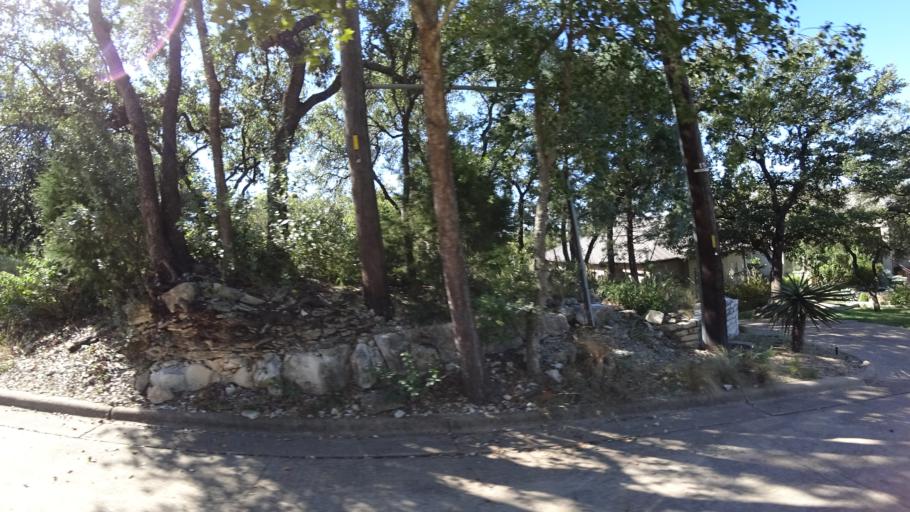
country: US
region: Texas
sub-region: Travis County
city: West Lake Hills
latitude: 30.3535
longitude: -97.7720
